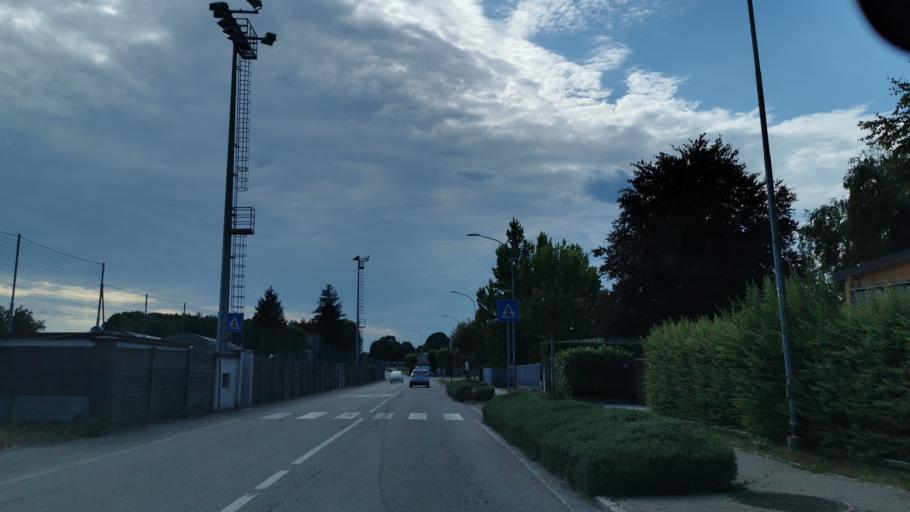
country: IT
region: Lombardy
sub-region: Provincia di Como
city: Orsenigo
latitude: 45.7782
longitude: 9.1773
